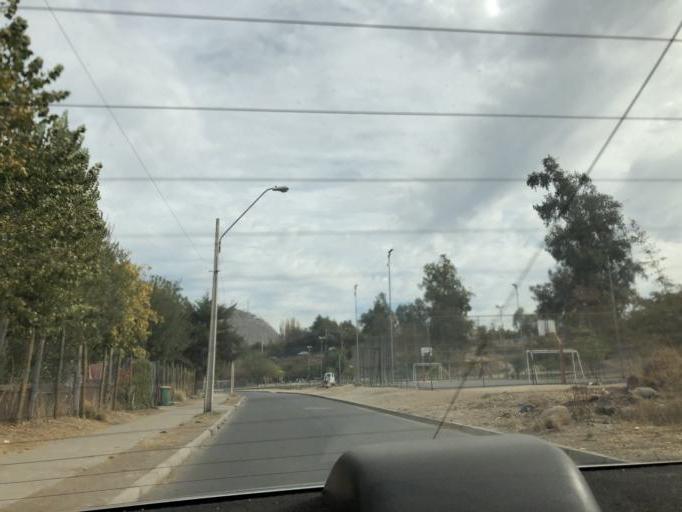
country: CL
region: Santiago Metropolitan
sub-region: Provincia de Cordillera
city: Puente Alto
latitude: -33.6069
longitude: -70.5328
